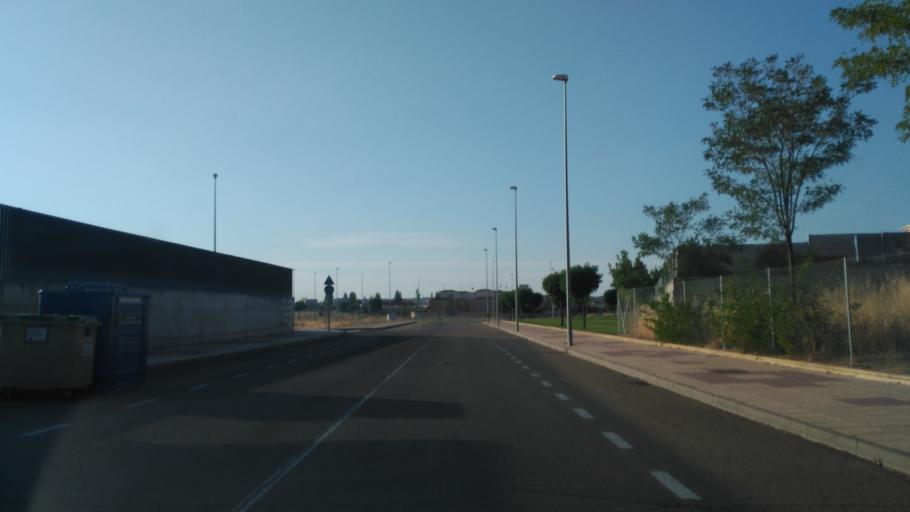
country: ES
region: Castille and Leon
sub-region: Provincia de Salamanca
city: Carbajosa de la Sagrada
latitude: 40.9365
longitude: -5.6439
